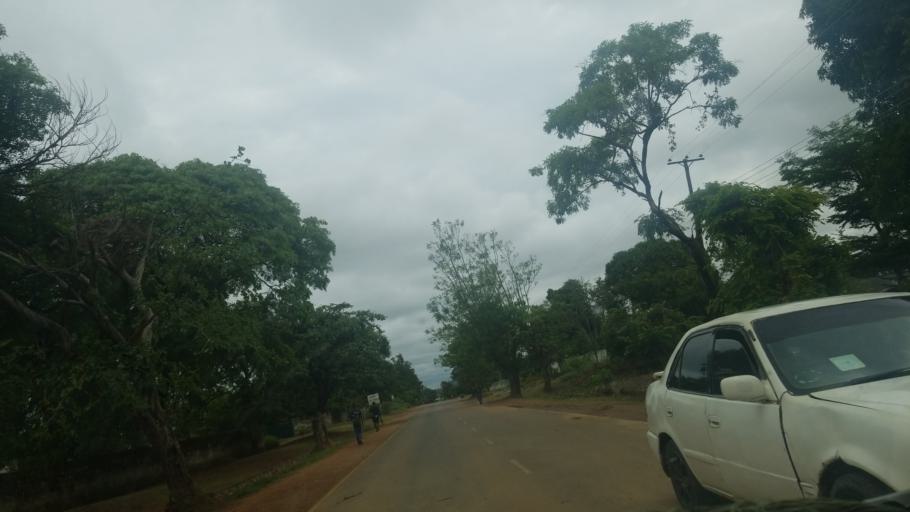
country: ZM
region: Luapula
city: Mansa
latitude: -11.1969
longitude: 28.8975
